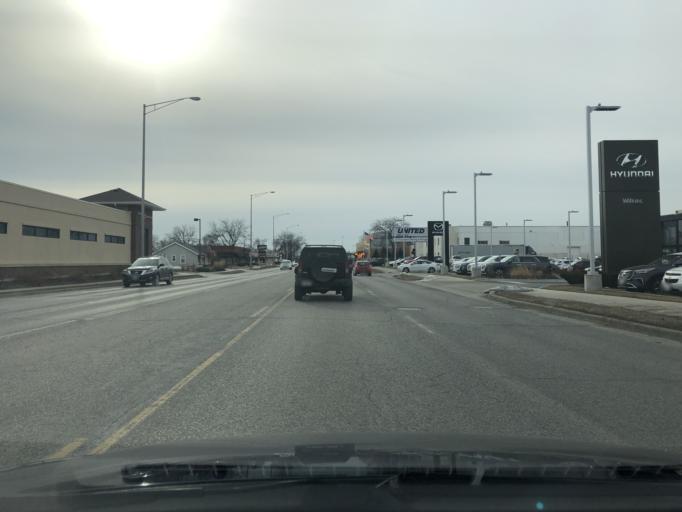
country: US
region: Illinois
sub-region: DuPage County
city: Elmhurst
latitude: 41.9227
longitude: -87.9399
